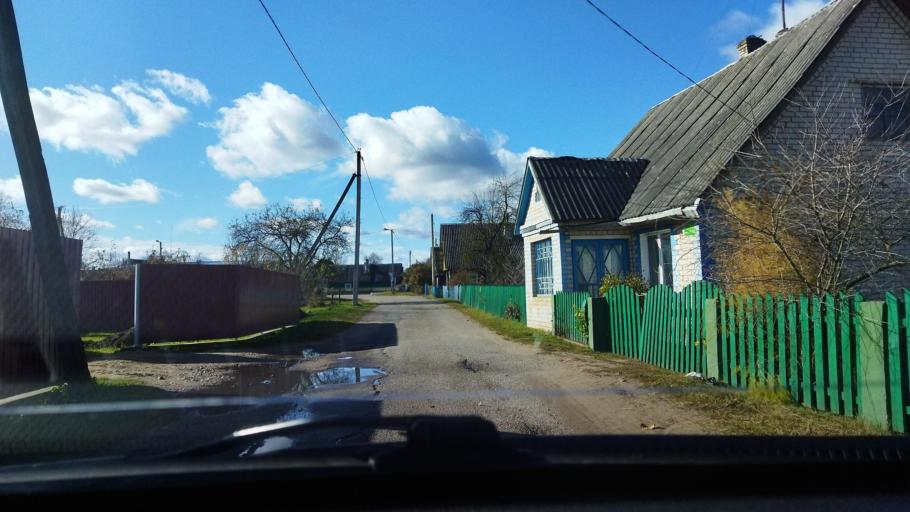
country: BY
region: Minsk
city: Svir
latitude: 54.8135
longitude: 26.1587
